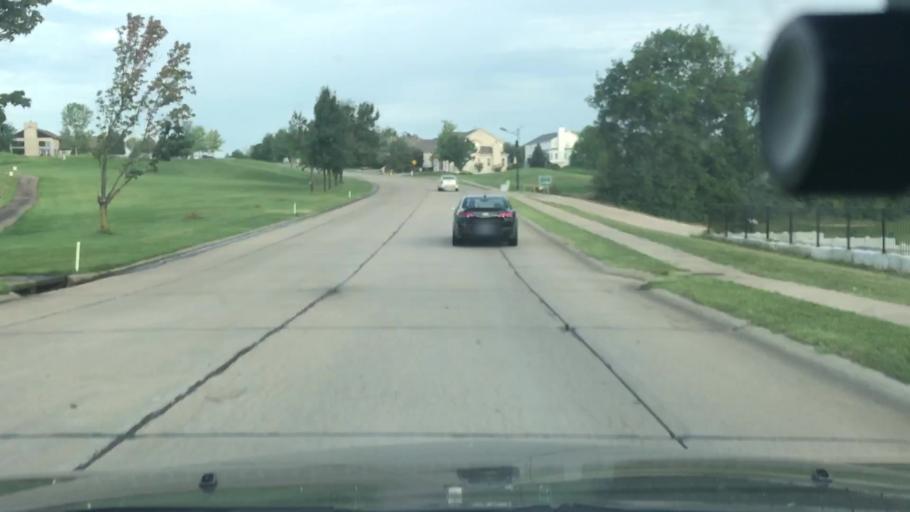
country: US
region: Missouri
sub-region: Saint Charles County
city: Wentzville
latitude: 38.8180
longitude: -90.8935
